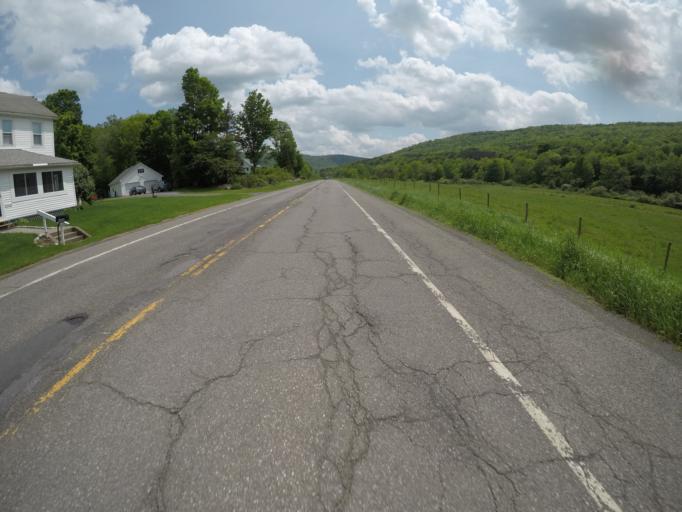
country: US
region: New York
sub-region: Delaware County
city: Stamford
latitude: 42.2349
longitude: -74.5985
